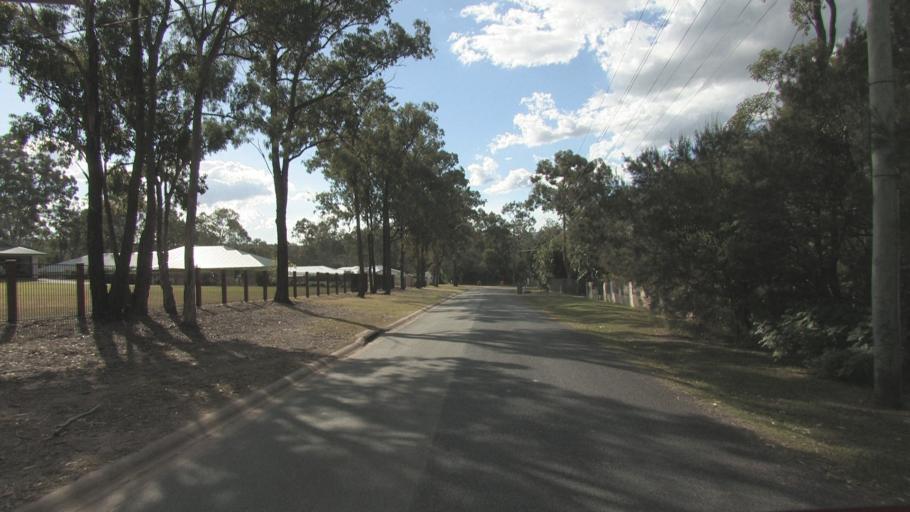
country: AU
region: Queensland
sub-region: Logan
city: Beenleigh
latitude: -27.6662
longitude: 153.2216
